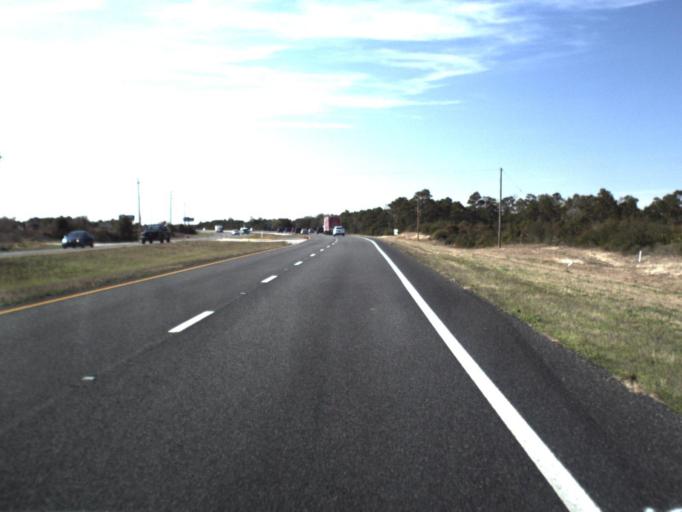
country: US
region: Florida
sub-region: Bay County
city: Laguna Beach
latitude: 30.2597
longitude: -85.9515
